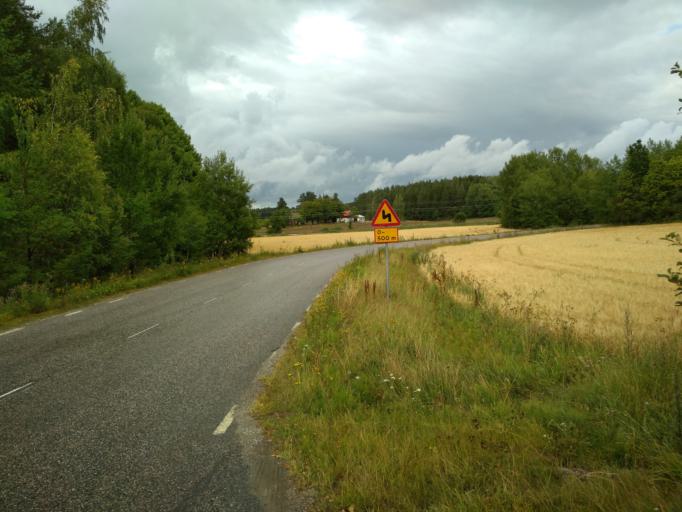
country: SE
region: Vaestmanland
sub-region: Kungsors Kommun
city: Kungsoer
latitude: 59.4199
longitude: 16.1616
